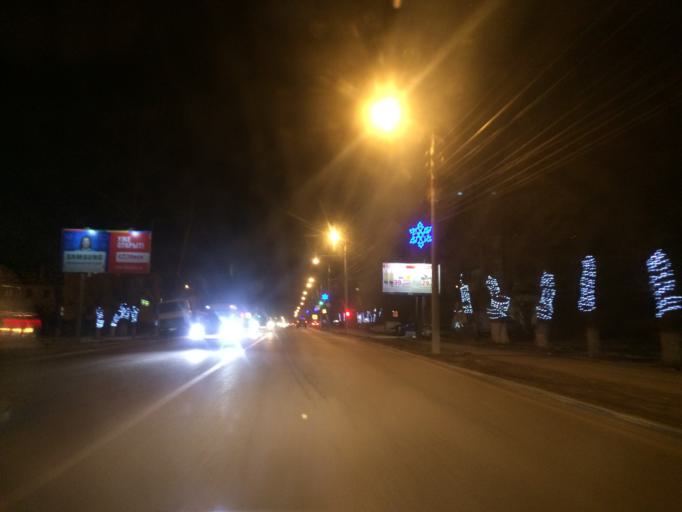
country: RU
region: Tula
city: Tula
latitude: 54.2062
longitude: 37.6753
